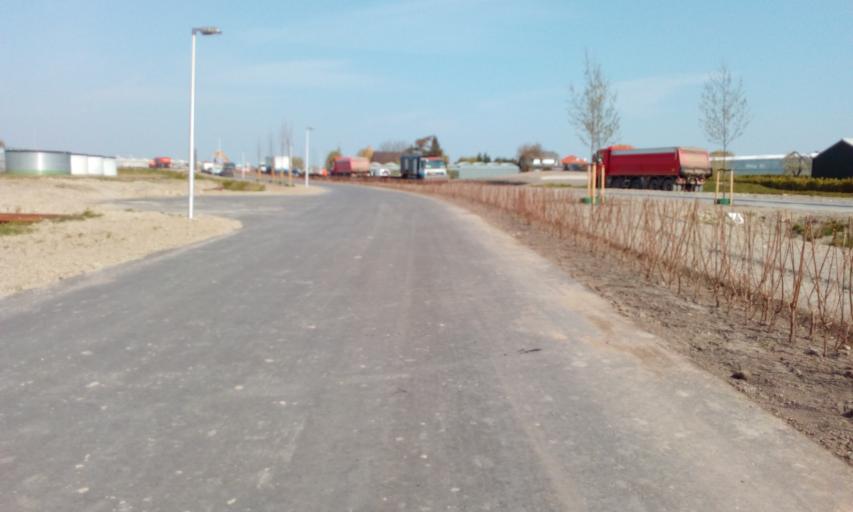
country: NL
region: South Holland
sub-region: Gemeente Pijnacker-Nootdorp
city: Pijnacker
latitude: 52.0127
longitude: 4.4141
